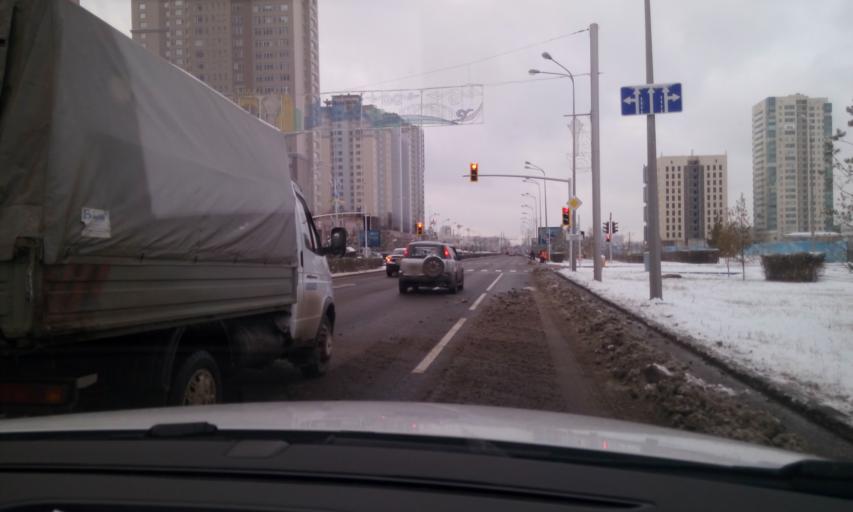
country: KZ
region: Astana Qalasy
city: Astana
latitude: 51.1286
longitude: 71.4648
